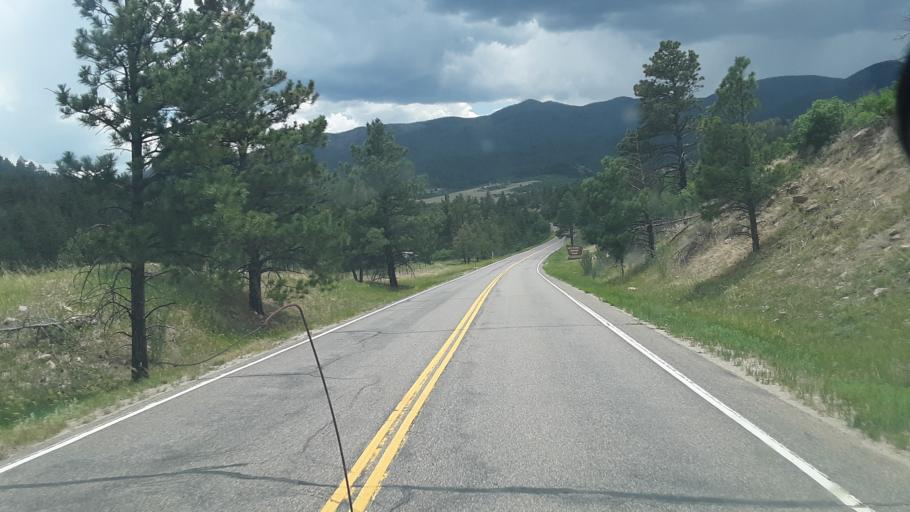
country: US
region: Colorado
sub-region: Fremont County
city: Florence
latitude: 38.1956
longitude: -105.1032
